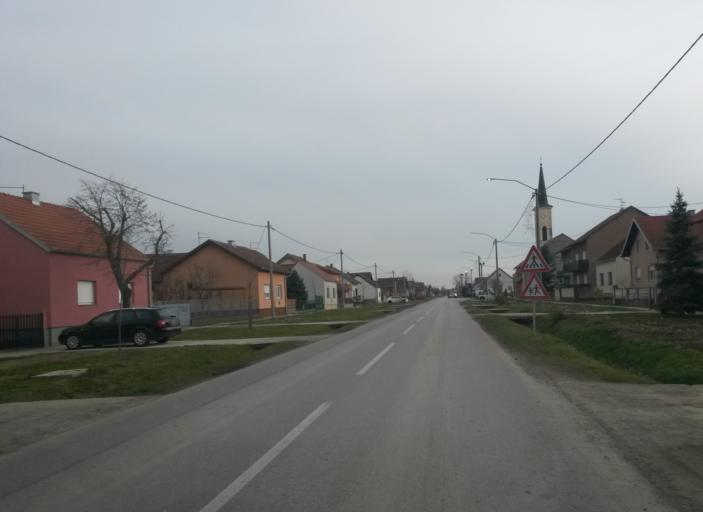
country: HR
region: Osjecko-Baranjska
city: Antunovac
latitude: 45.4869
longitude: 18.6345
